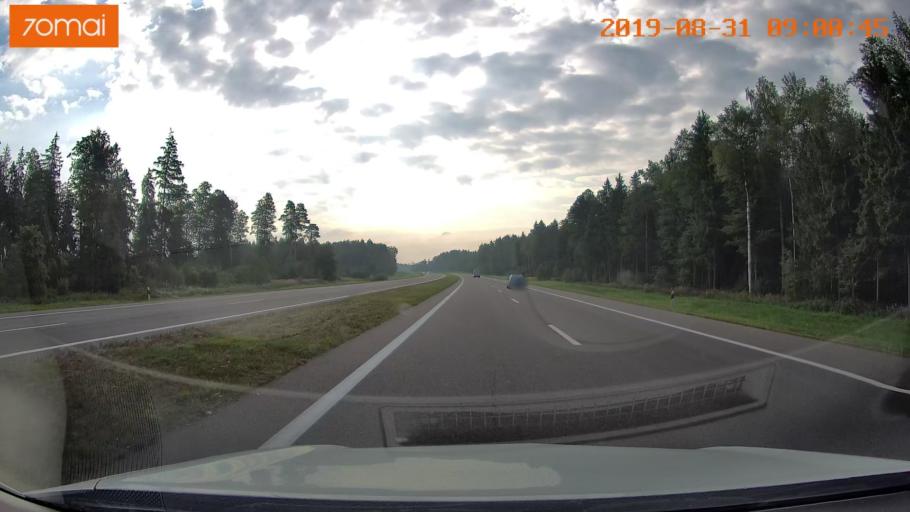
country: BY
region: Minsk
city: Chervyen'
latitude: 53.7541
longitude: 28.2438
